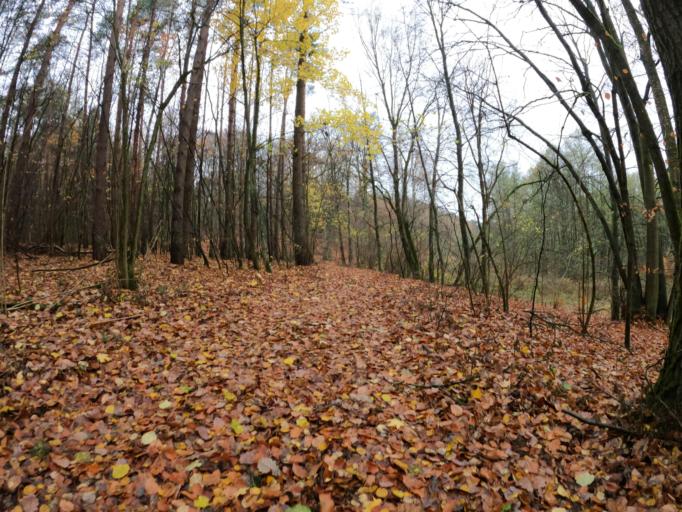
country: PL
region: West Pomeranian Voivodeship
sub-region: Powiat walecki
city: Tuczno
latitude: 53.2664
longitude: 16.2567
